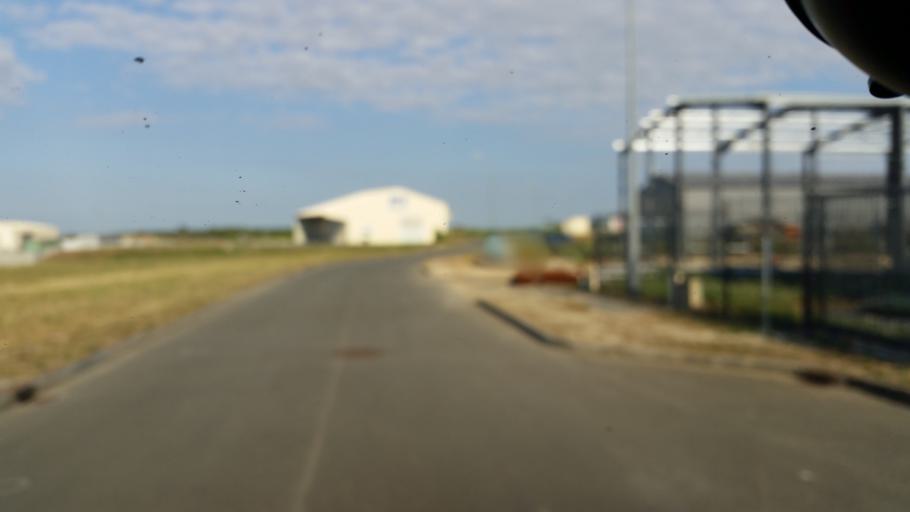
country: FR
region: Poitou-Charentes
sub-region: Departement de la Charente-Maritime
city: Saint-Jean-de-Liversay
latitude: 46.2318
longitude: -0.8827
